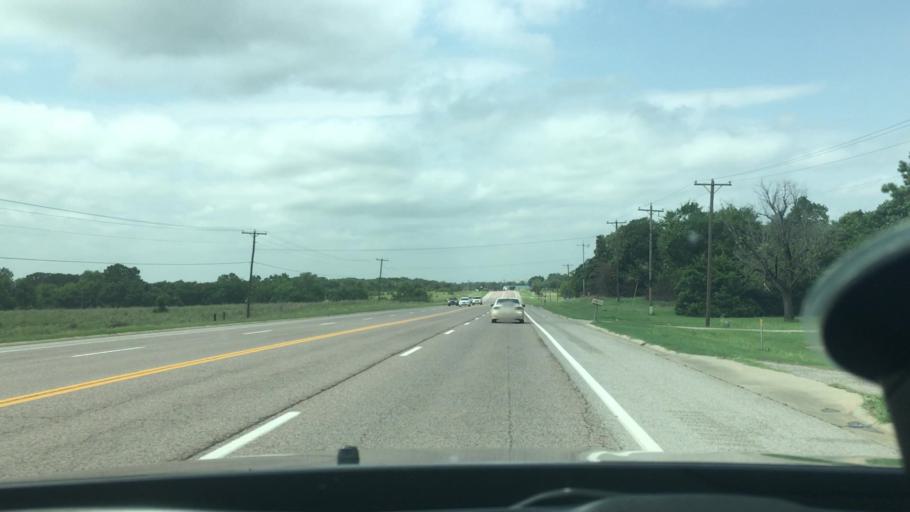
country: US
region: Oklahoma
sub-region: Pontotoc County
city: Ada
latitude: 34.7940
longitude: -96.7334
